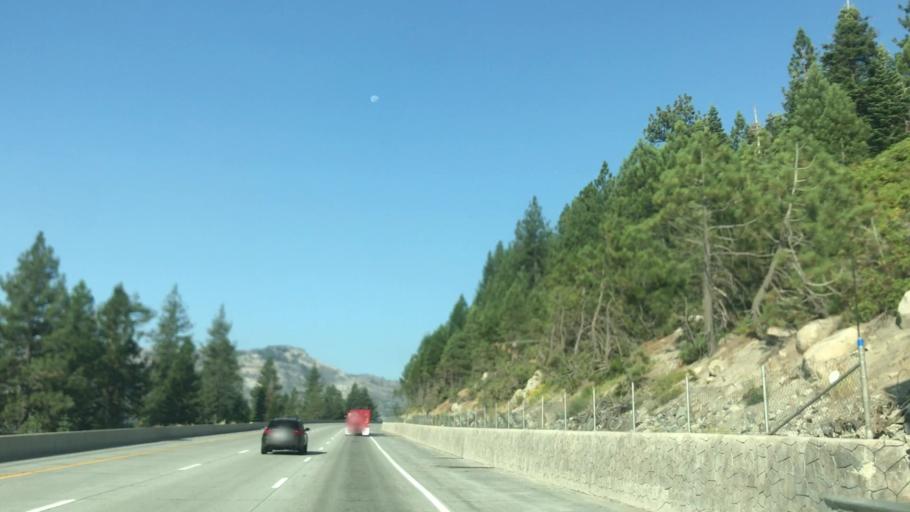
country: US
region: California
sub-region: Nevada County
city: Truckee
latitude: 39.3289
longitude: -120.2692
